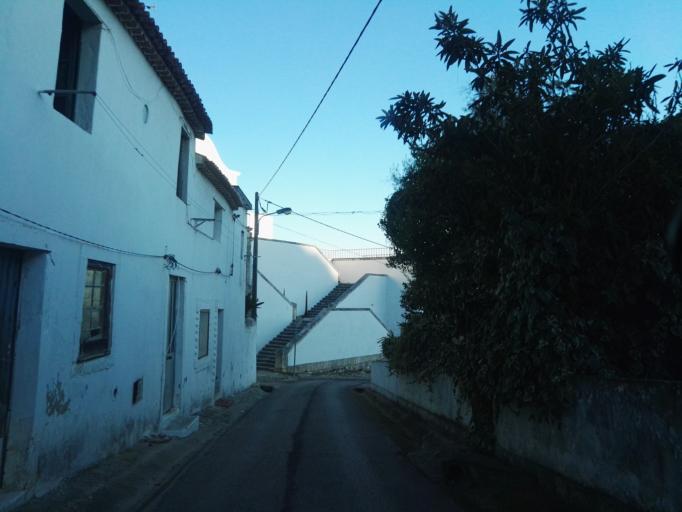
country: PT
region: Santarem
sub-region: Santarem
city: Santarem
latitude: 39.2316
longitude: -8.6759
